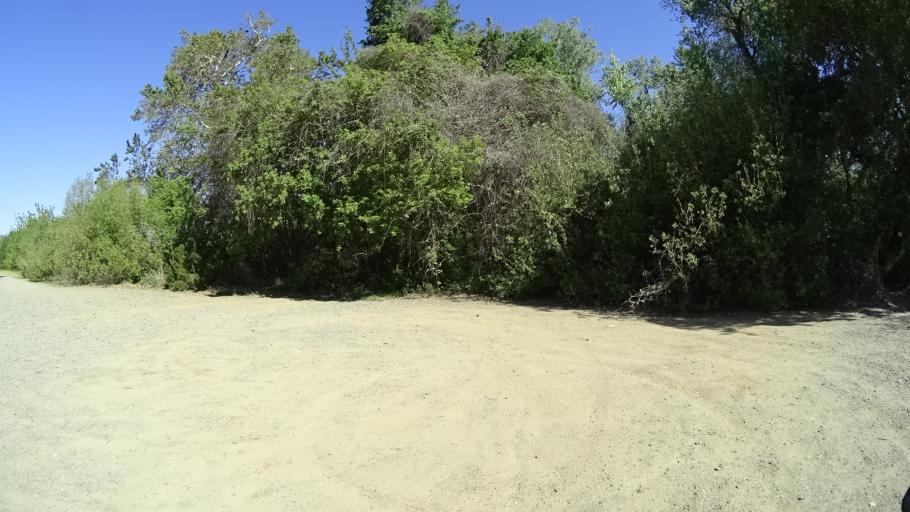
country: US
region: California
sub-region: Glenn County
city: Hamilton City
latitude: 39.7126
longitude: -121.9518
